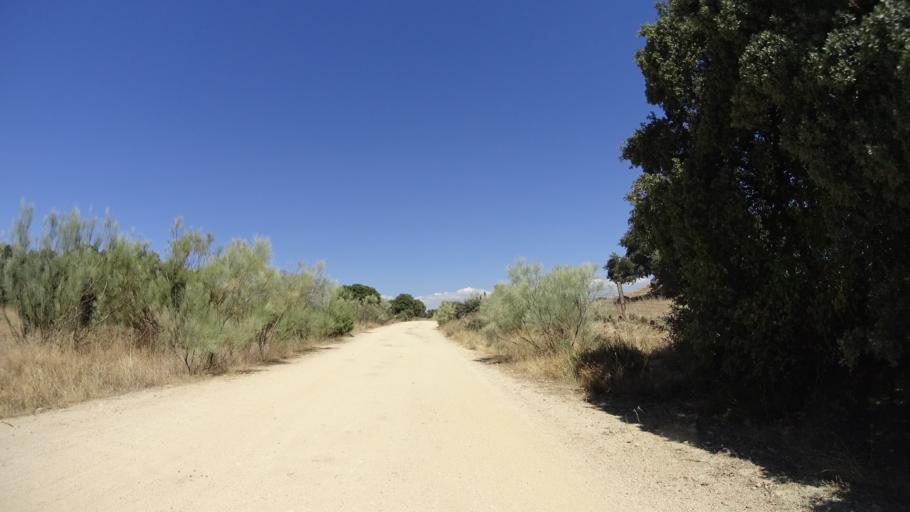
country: ES
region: Madrid
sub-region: Provincia de Madrid
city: Colmenarejo
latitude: 40.5334
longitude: -4.0108
